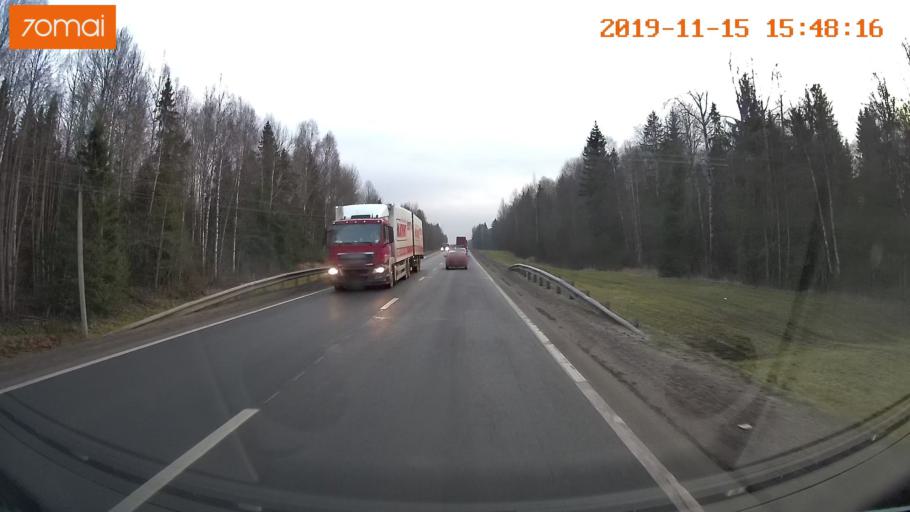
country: RU
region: Jaroslavl
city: Danilov
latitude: 57.9292
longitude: 40.0065
